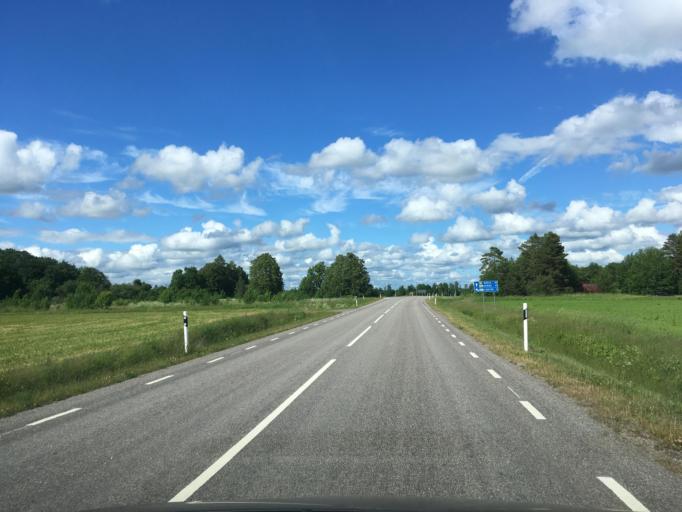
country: EE
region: Paernumaa
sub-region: Halinga vald
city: Parnu-Jaagupi
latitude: 58.6451
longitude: 24.5599
